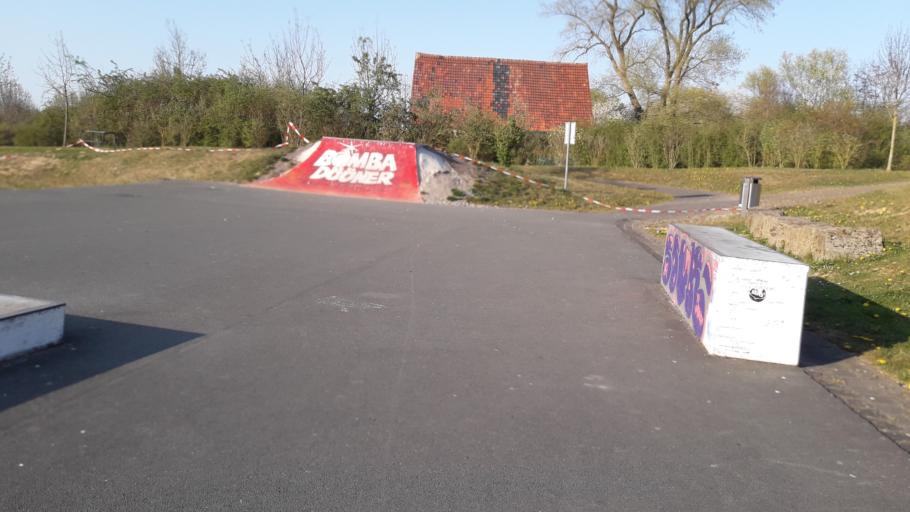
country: DE
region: North Rhine-Westphalia
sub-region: Regierungsbezirk Detmold
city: Paderborn
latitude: 51.7142
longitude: 8.8045
